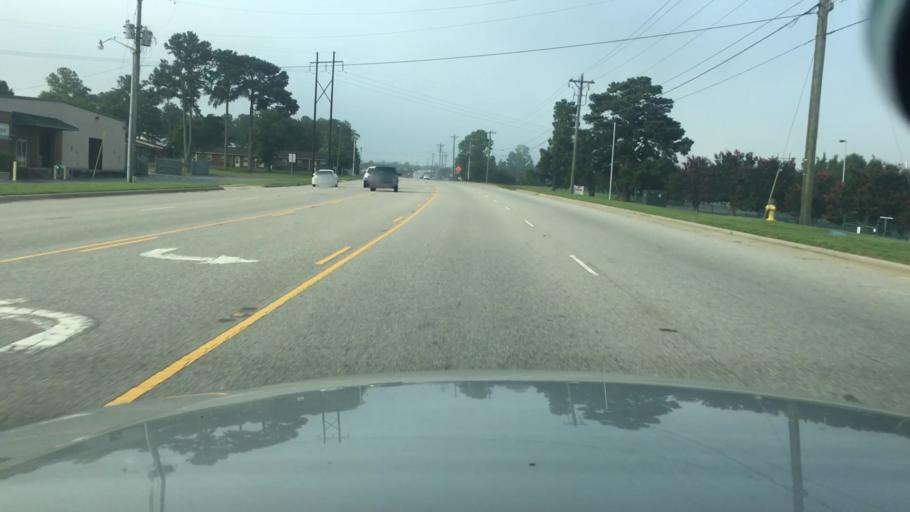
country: US
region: North Carolina
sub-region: Cumberland County
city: Hope Mills
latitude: 35.0123
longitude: -78.9190
